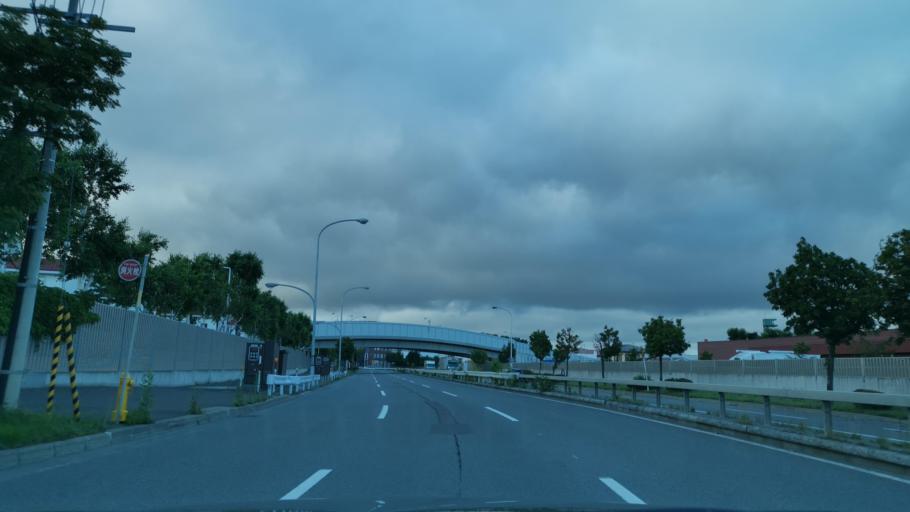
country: JP
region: Hokkaido
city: Sapporo
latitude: 43.0778
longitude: 141.3223
